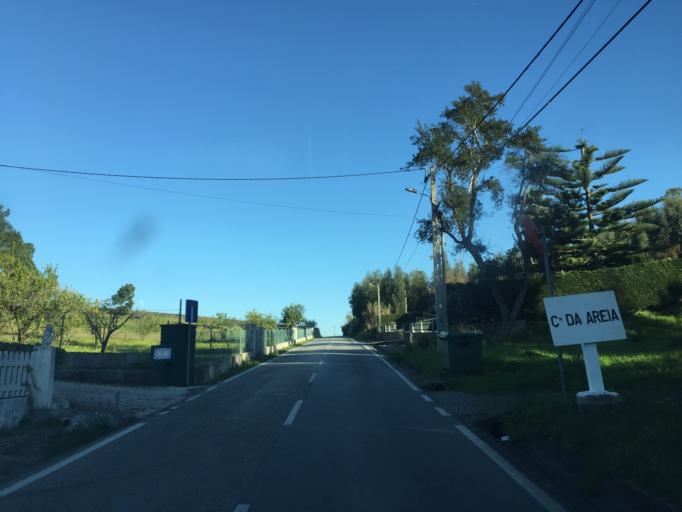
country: PT
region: Coimbra
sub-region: Figueira da Foz
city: Tavarede
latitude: 40.1658
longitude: -8.8242
